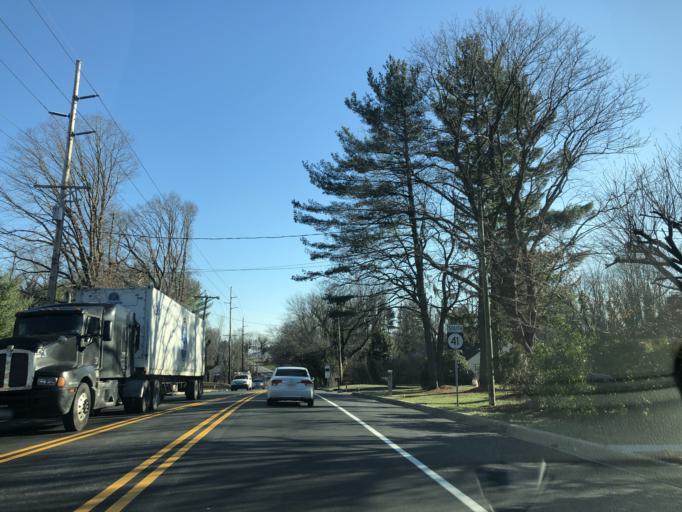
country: US
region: Delaware
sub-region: New Castle County
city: Elsmere
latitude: 39.7453
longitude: -75.6445
